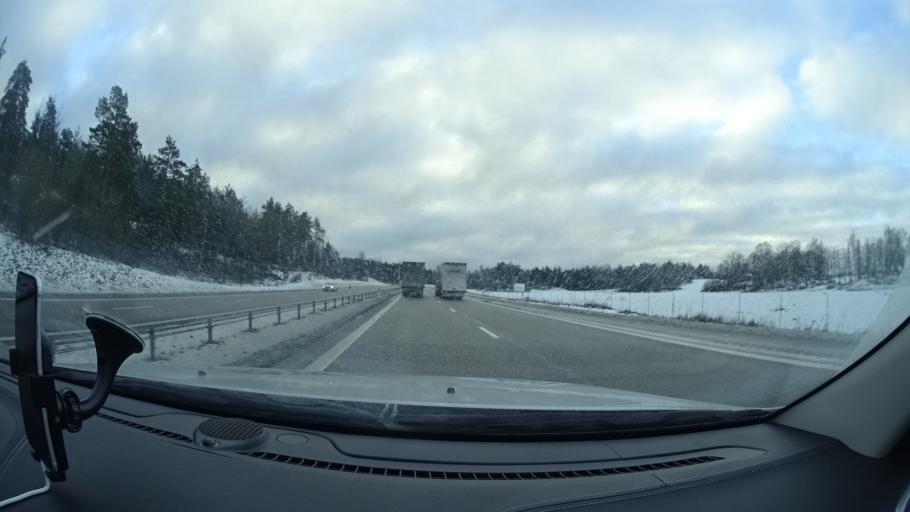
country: SE
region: OEstergoetland
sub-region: Odeshogs Kommun
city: OEdeshoeg
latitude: 58.2158
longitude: 14.6471
